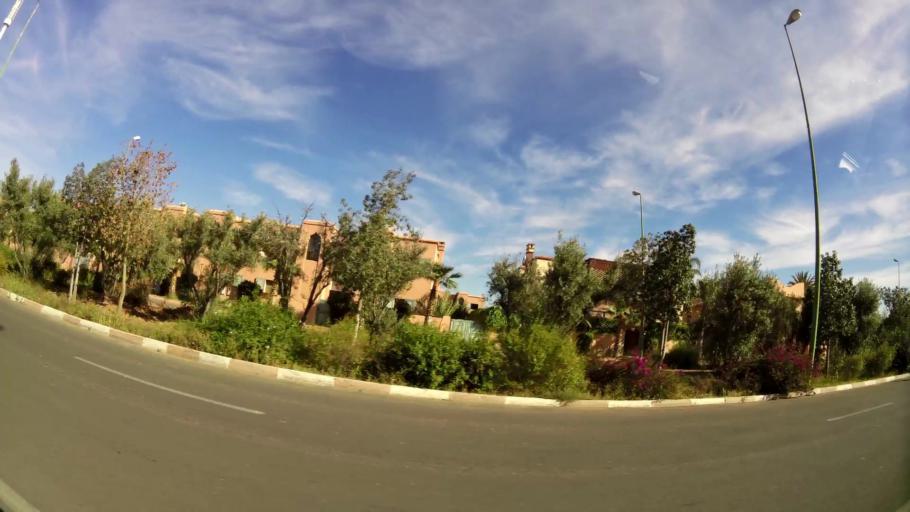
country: MA
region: Marrakech-Tensift-Al Haouz
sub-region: Marrakech
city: Marrakesh
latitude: 31.6783
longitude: -8.0554
